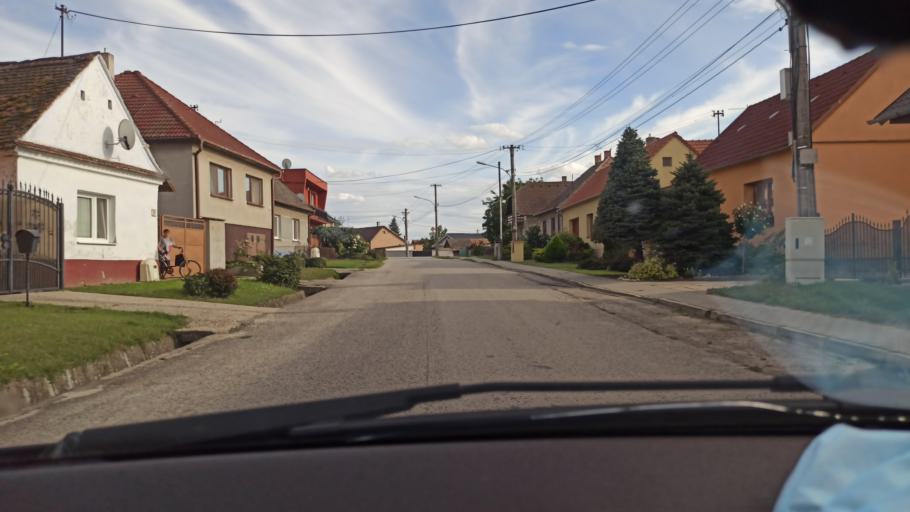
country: SK
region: Trnavsky
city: Gbely
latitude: 48.6734
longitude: 17.2038
